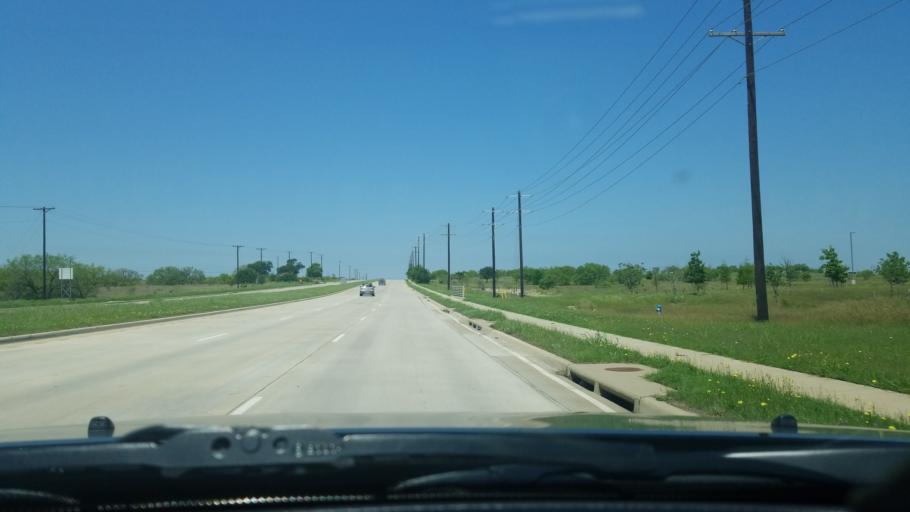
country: US
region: Texas
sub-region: Denton County
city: Krum
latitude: 33.2311
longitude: -97.2018
